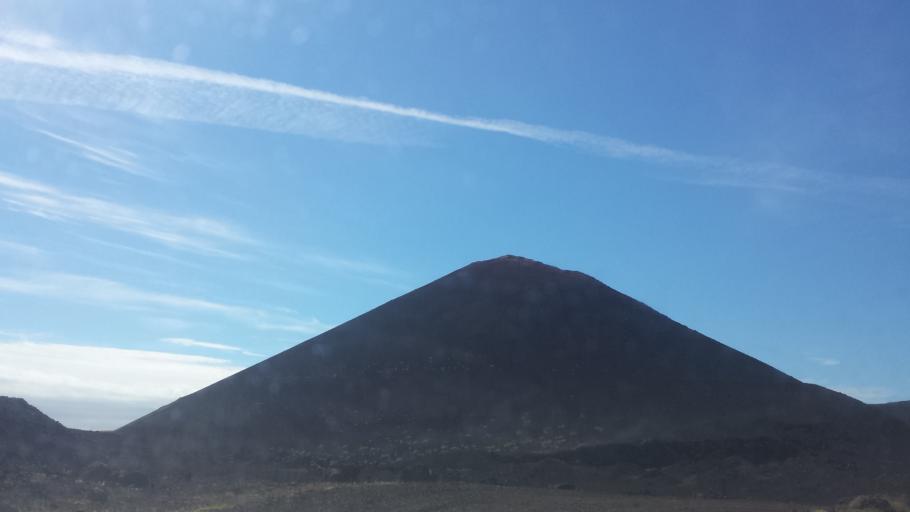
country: IS
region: South
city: Vestmannaeyjar
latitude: 63.4361
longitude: -20.2390
